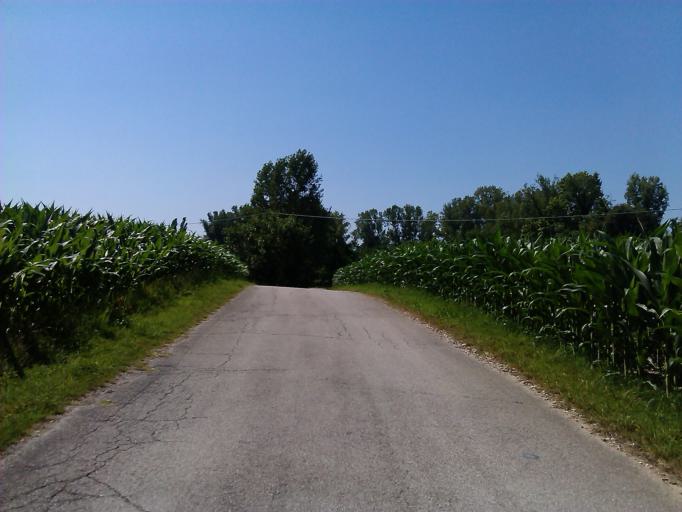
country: IT
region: Veneto
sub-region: Provincia di Treviso
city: Loria Bessica
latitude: 45.7249
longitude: 11.8744
